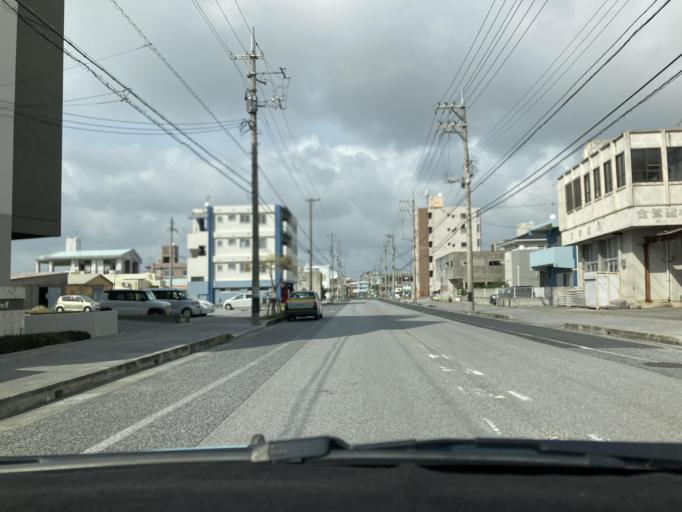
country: JP
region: Okinawa
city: Itoman
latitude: 26.1201
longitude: 127.6693
